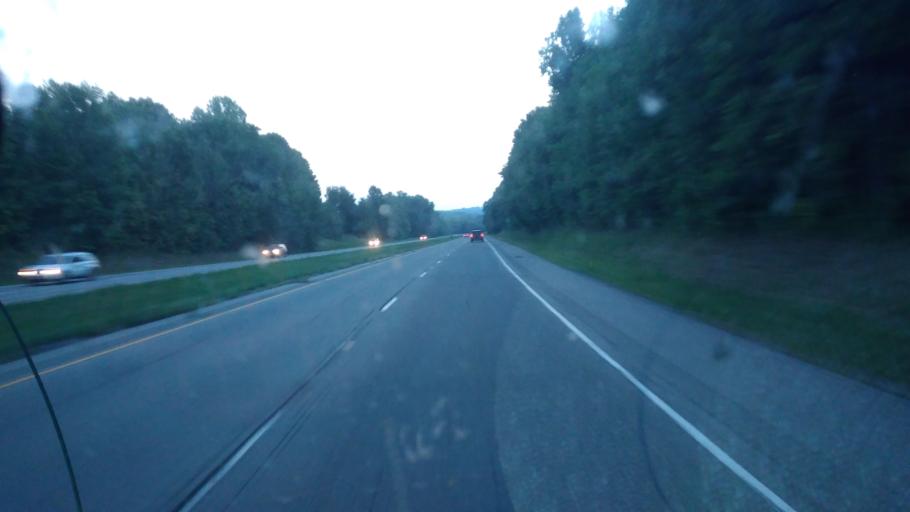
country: US
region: Ohio
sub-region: Richland County
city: Mansfield
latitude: 40.7205
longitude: -82.5026
